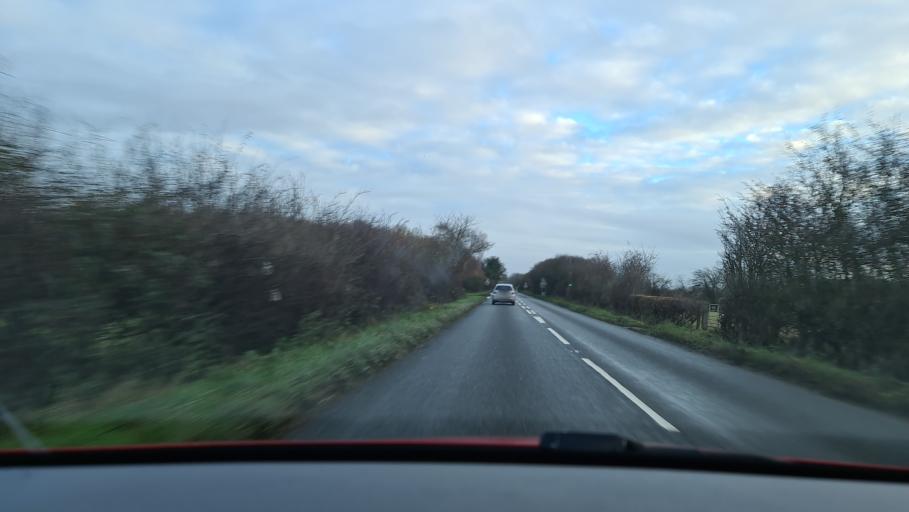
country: GB
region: England
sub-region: Buckinghamshire
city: Princes Risborough
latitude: 51.7420
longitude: -0.8331
